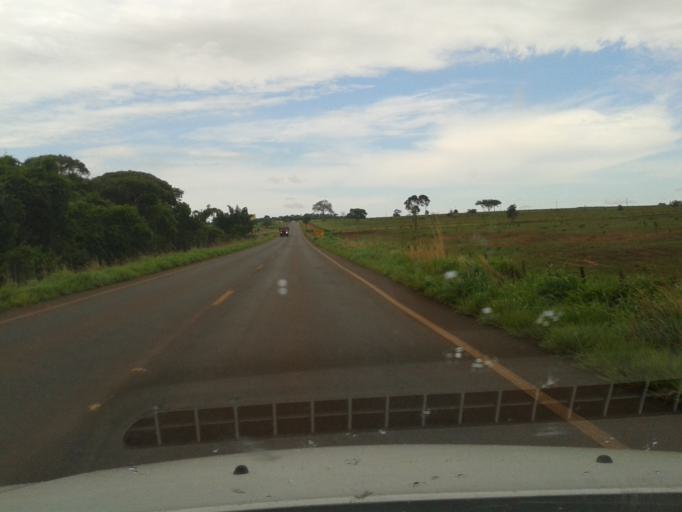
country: BR
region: Minas Gerais
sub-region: Iturama
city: Iturama
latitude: -19.6951
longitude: -50.1629
